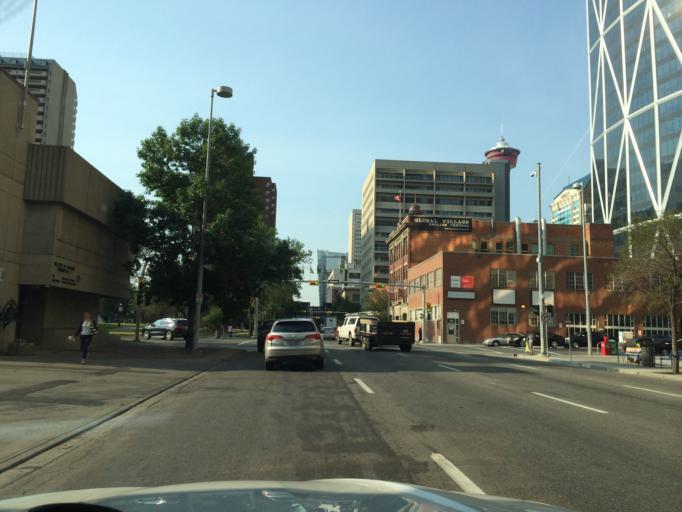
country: CA
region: Alberta
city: Calgary
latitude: 51.0488
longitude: -114.0603
